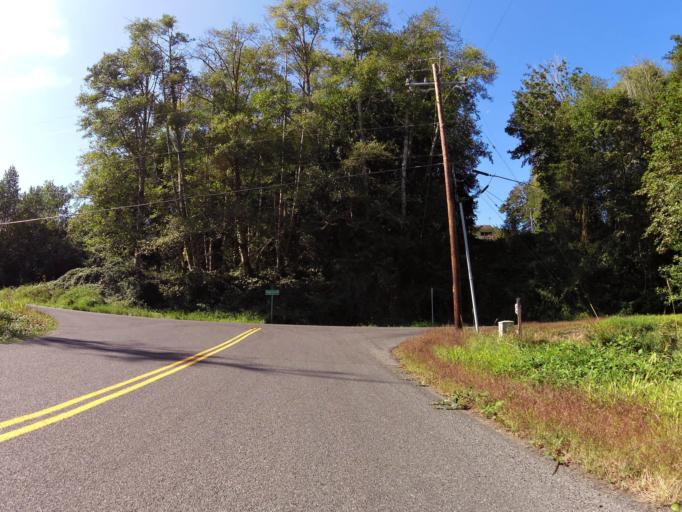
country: US
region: Washington
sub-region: Wahkiakum County
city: Cathlamet
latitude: 46.1826
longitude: -123.5833
